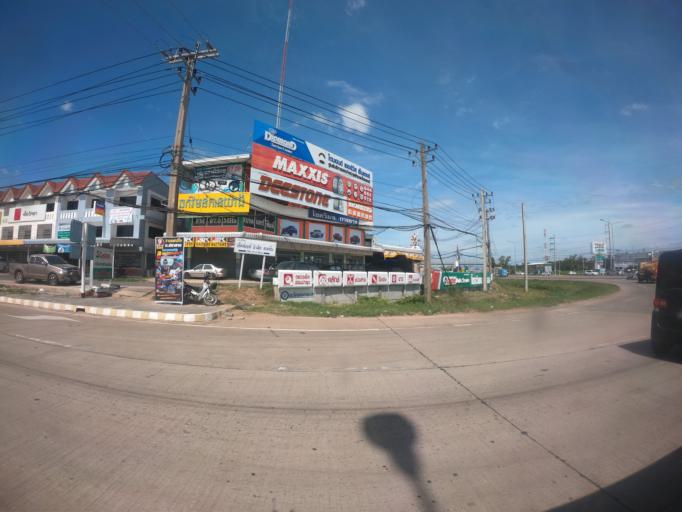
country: TH
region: Surin
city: Prasat
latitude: 14.6302
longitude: 103.4087
